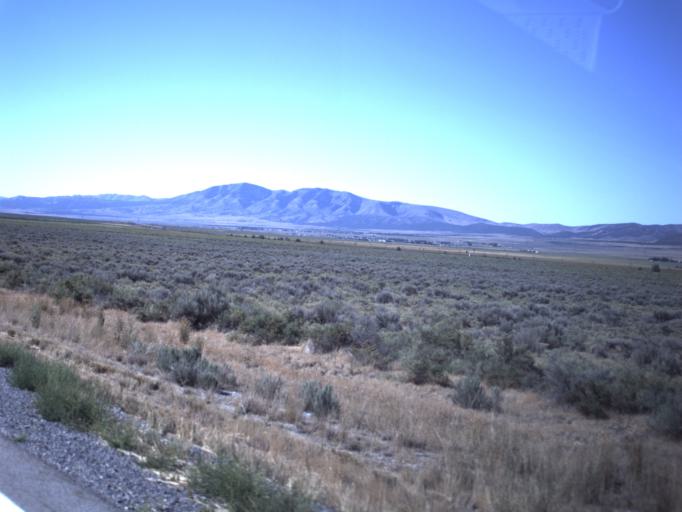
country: US
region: Utah
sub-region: Tooele County
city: Tooele
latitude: 40.4048
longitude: -112.3858
